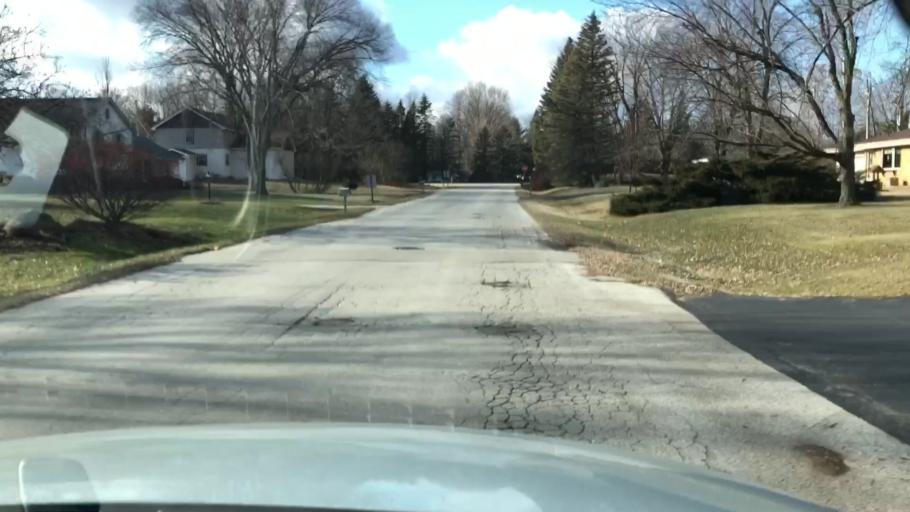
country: US
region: Wisconsin
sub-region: Waukesha County
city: Waukesha
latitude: 43.0680
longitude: -88.1844
